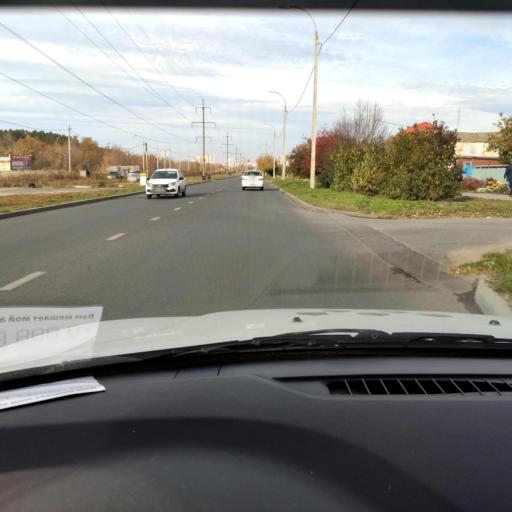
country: RU
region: Samara
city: Tol'yatti
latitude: 53.5164
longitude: 49.3953
